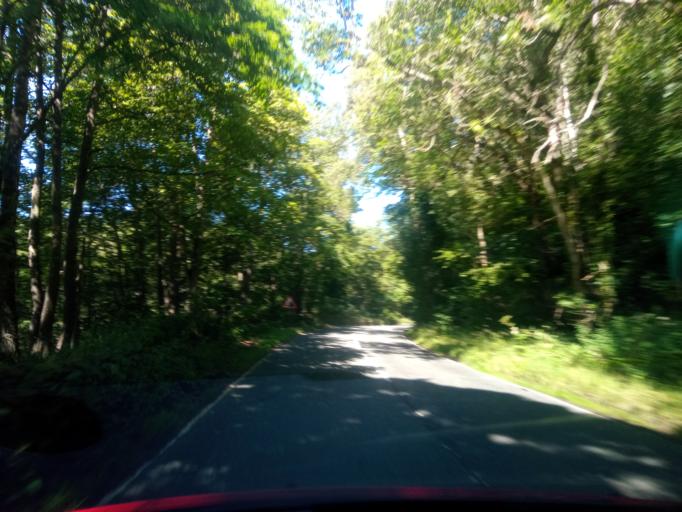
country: GB
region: England
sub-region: Northumberland
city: Bardon Mill
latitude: 54.9244
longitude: -2.3112
